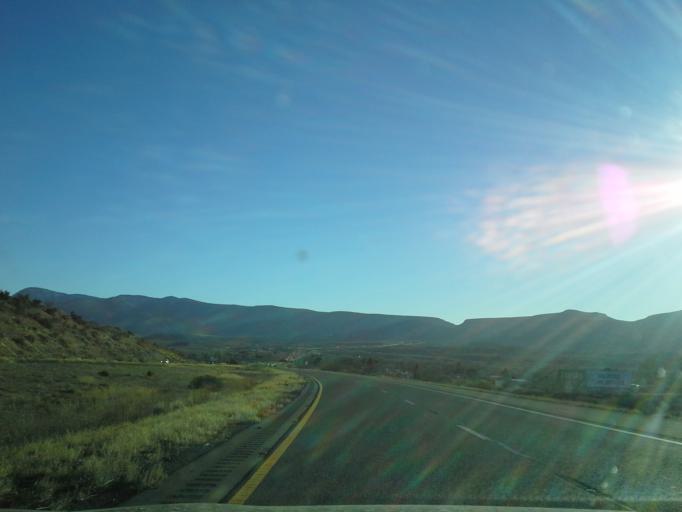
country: US
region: Arizona
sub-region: Yavapai County
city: Camp Verde
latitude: 34.6066
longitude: -111.8694
